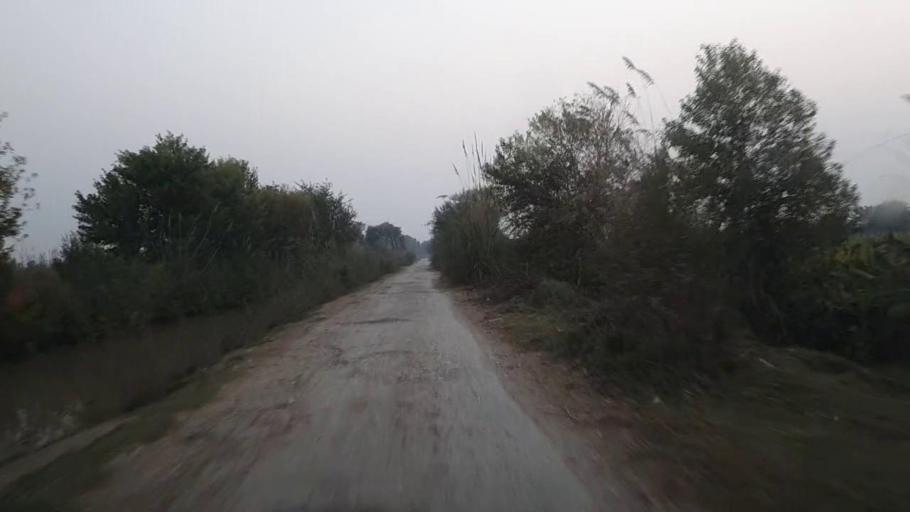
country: PK
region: Sindh
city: Karaundi
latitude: 26.9343
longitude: 68.4417
